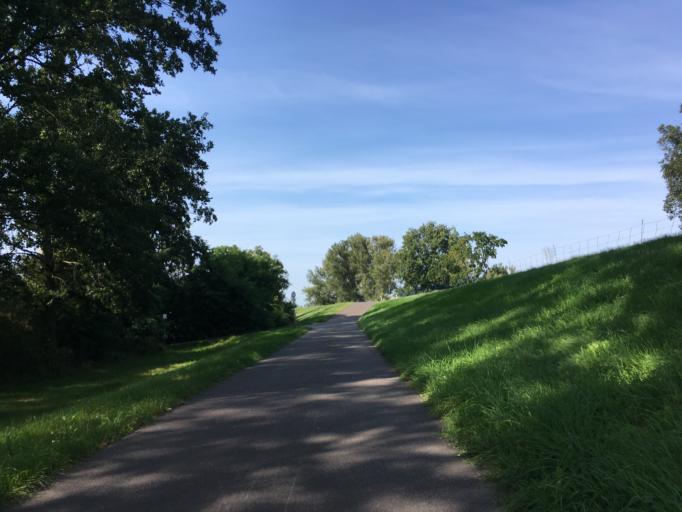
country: DE
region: Brandenburg
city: Vogelsang
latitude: 52.1748
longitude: 14.7003
